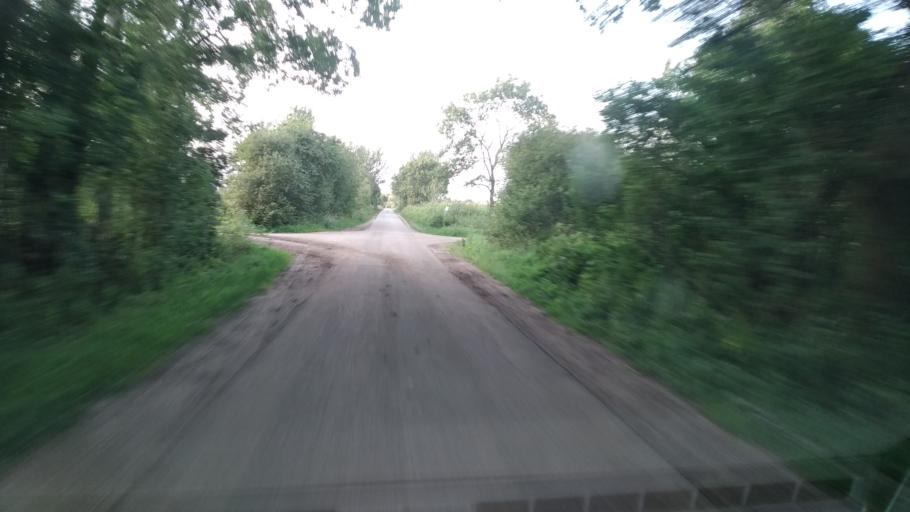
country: DE
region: Schleswig-Holstein
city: Klein Bennebek
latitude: 54.4092
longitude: 9.4593
